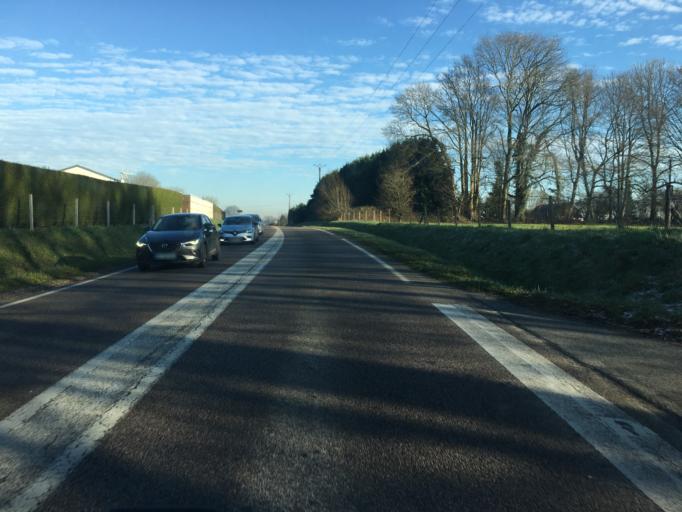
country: FR
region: Haute-Normandie
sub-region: Departement de la Seine-Maritime
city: Sainte-Marie-des-Champs
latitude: 49.6118
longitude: 0.7790
